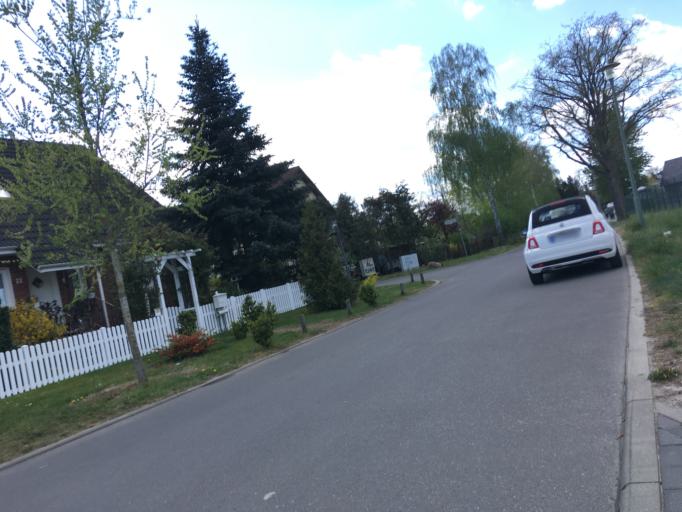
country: DE
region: Berlin
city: Mahlsdorf
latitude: 52.5163
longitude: 13.6351
